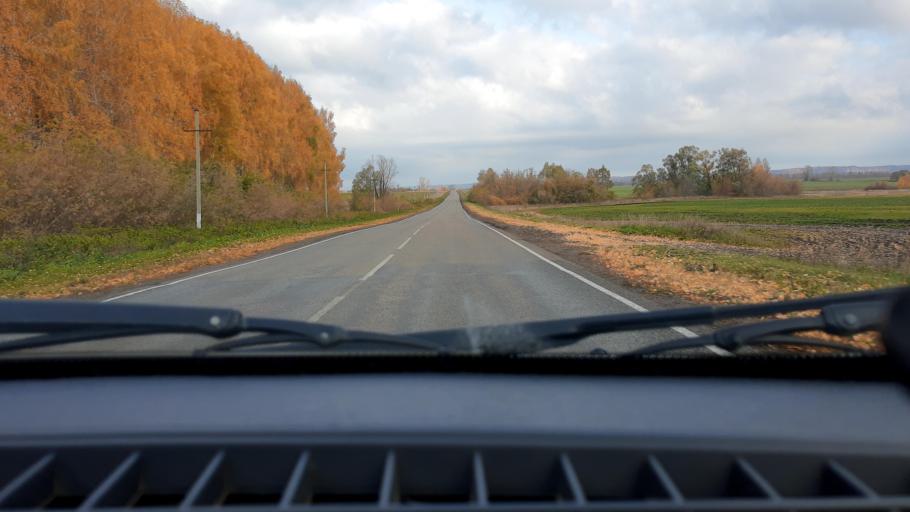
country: RU
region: Bashkortostan
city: Ulukulevo
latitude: 54.3993
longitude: 56.3783
